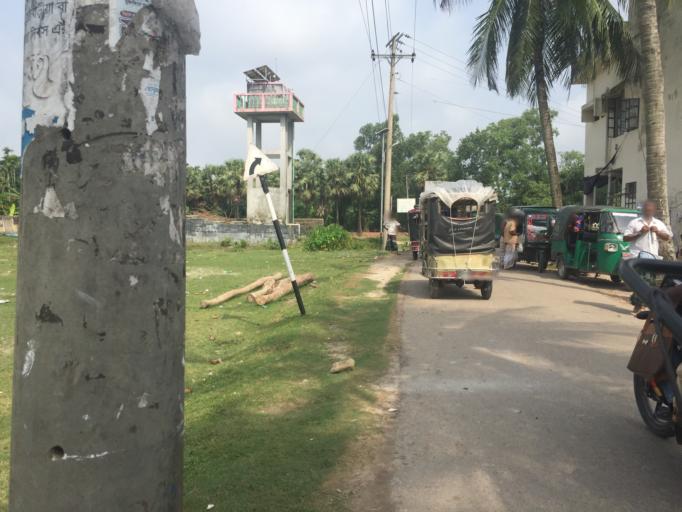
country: BD
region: Barisal
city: Mathba
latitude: 22.2451
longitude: 89.9134
